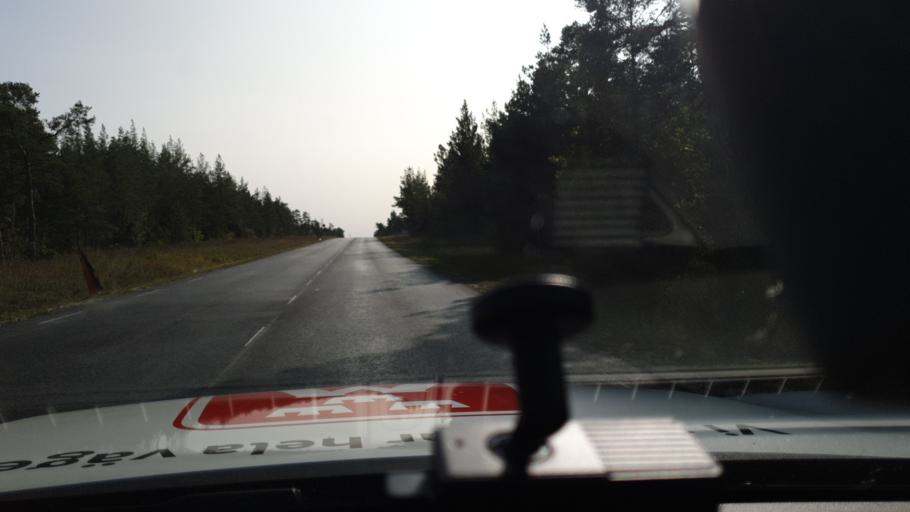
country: SE
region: Gotland
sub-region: Gotland
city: Slite
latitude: 57.7534
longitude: 18.7904
